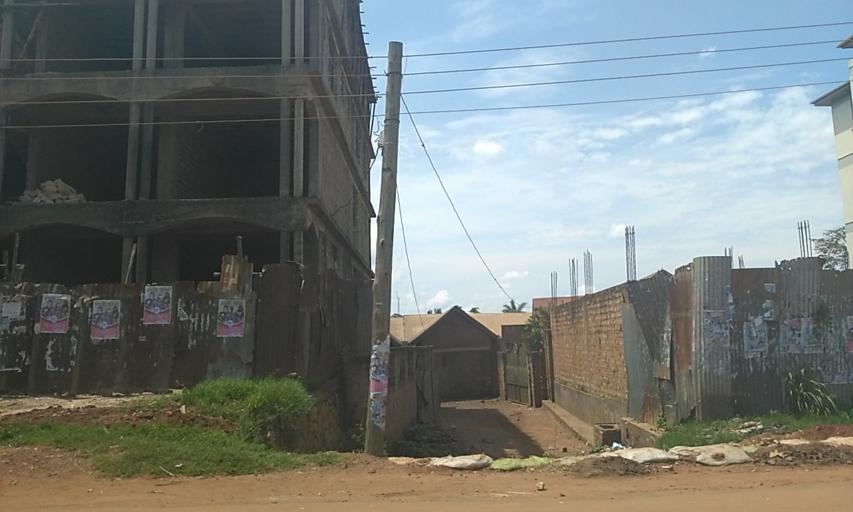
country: UG
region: Central Region
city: Kampala Central Division
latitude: 0.3600
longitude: 32.5314
